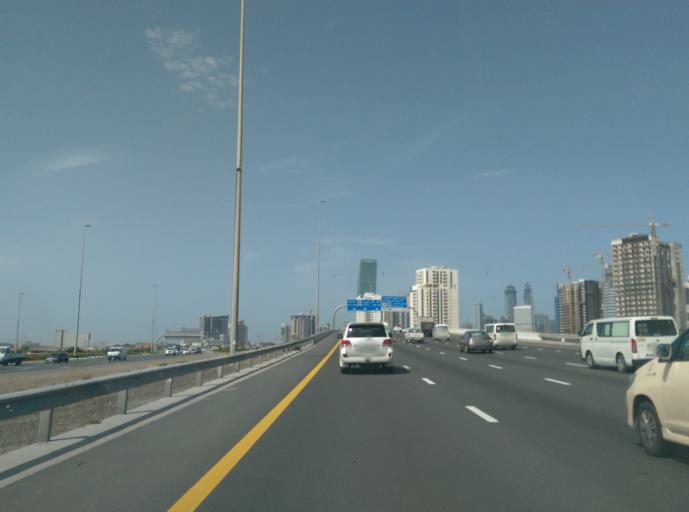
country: AE
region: Dubai
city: Dubai
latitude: 25.1830
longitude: 55.2895
